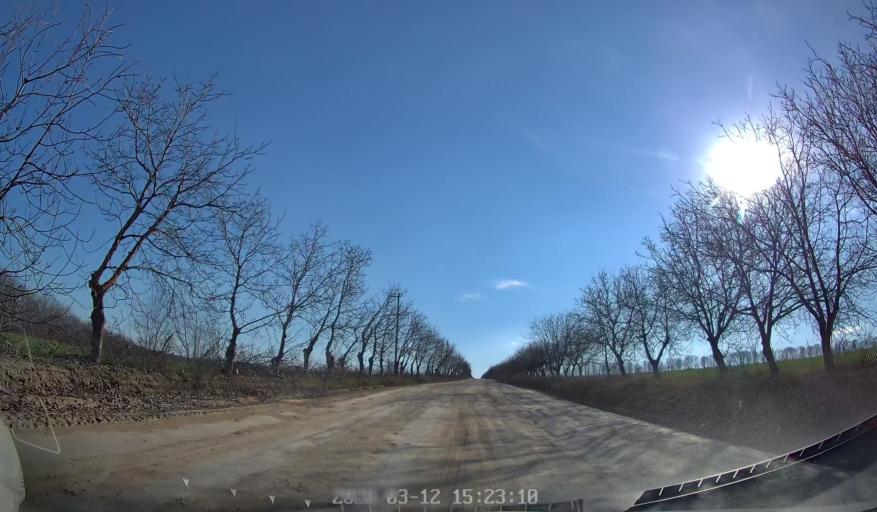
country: MD
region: Chisinau
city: Ciorescu
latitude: 47.1933
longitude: 28.9173
